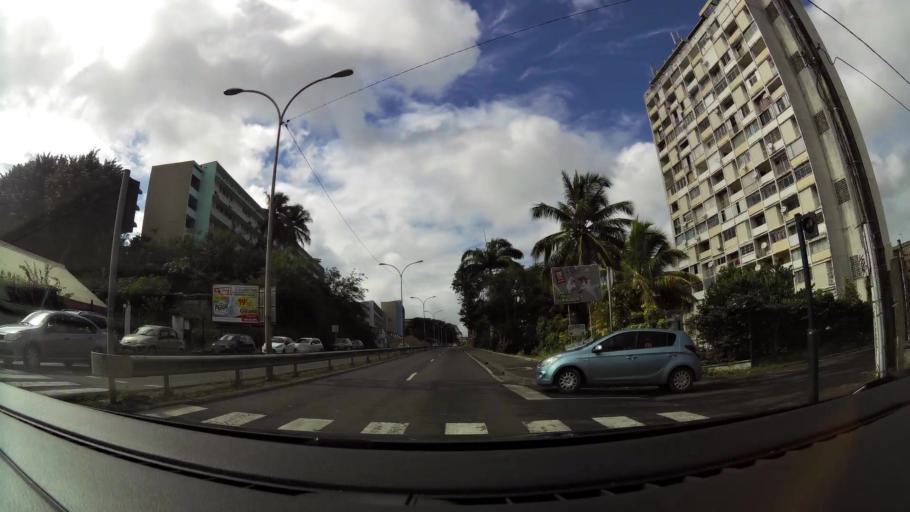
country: GP
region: Guadeloupe
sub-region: Guadeloupe
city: Pointe-a-Pitre
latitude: 16.2504
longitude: -61.5228
